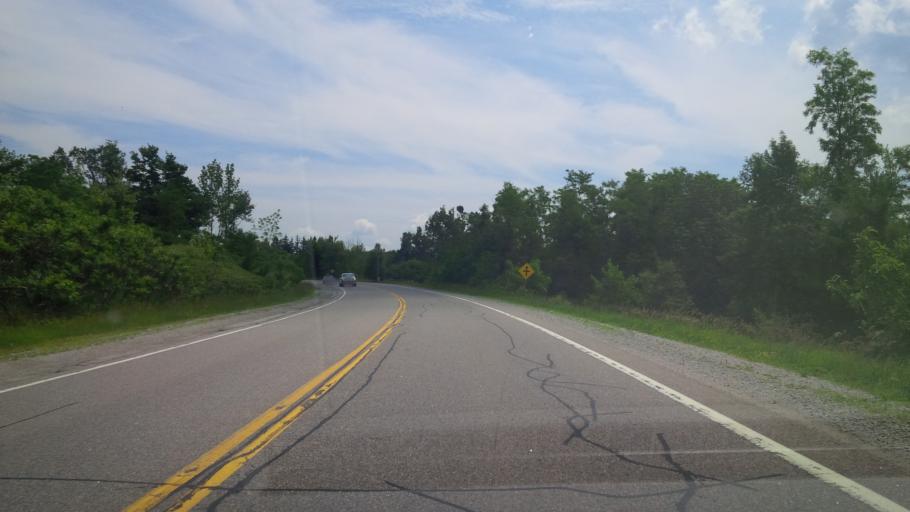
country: CA
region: Ontario
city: Burlington
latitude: 43.4068
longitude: -79.8779
